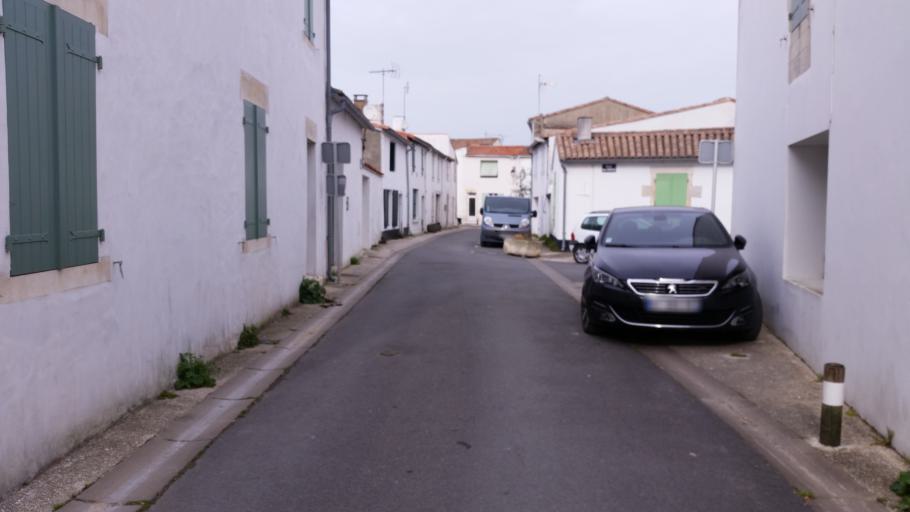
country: FR
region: Poitou-Charentes
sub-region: Departement de la Charente-Maritime
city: La Flotte
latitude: 46.1860
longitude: -1.3239
